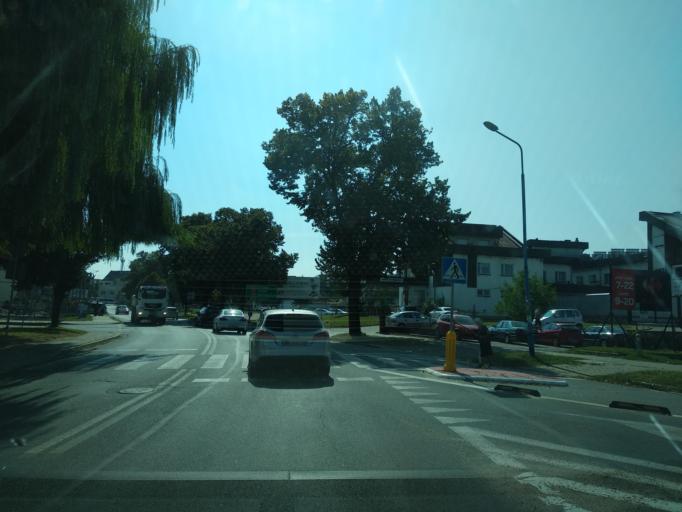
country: PL
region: Lower Silesian Voivodeship
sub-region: Powiat strzelinski
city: Strzelin
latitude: 50.7861
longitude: 17.0694
